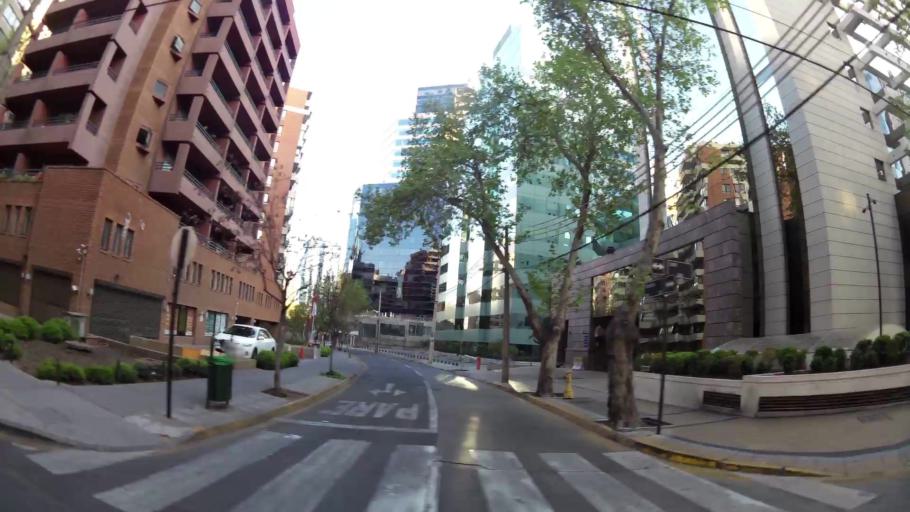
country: CL
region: Santiago Metropolitan
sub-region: Provincia de Santiago
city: Villa Presidente Frei, Nunoa, Santiago, Chile
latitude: -33.4153
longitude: -70.6022
